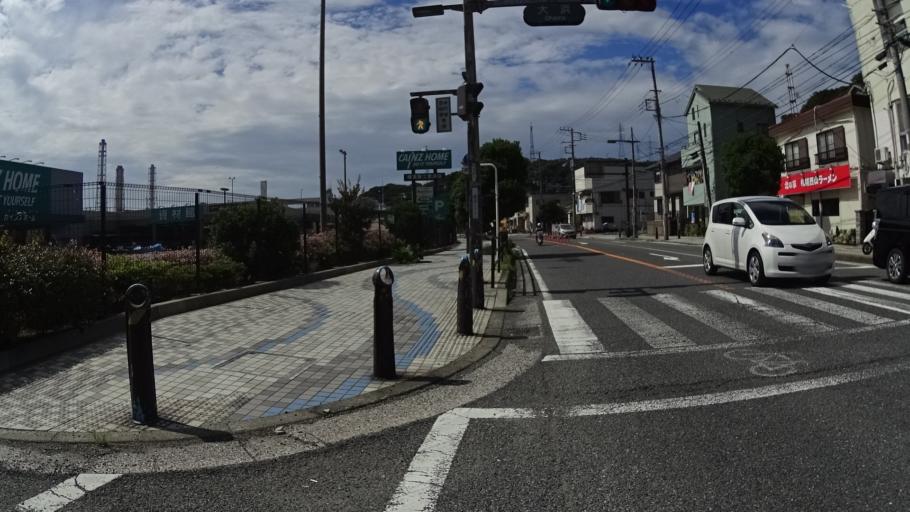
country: JP
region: Kanagawa
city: Yokosuka
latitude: 35.2227
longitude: 139.7120
